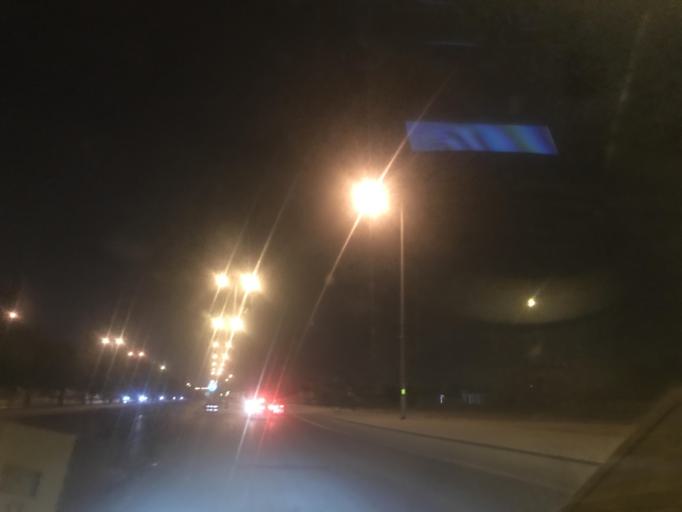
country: SA
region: Ar Riyad
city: Riyadh
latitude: 24.7939
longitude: 46.5869
